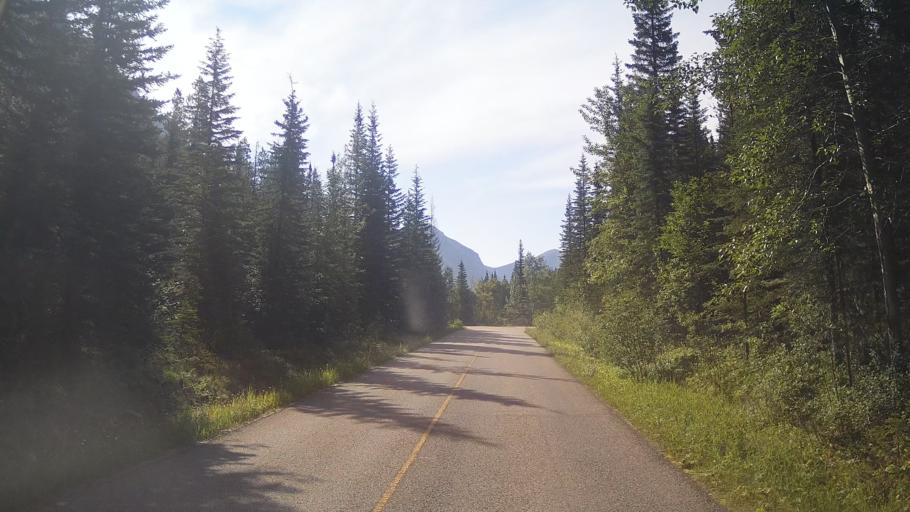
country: CA
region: Alberta
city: Hinton
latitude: 53.1748
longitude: -117.8292
